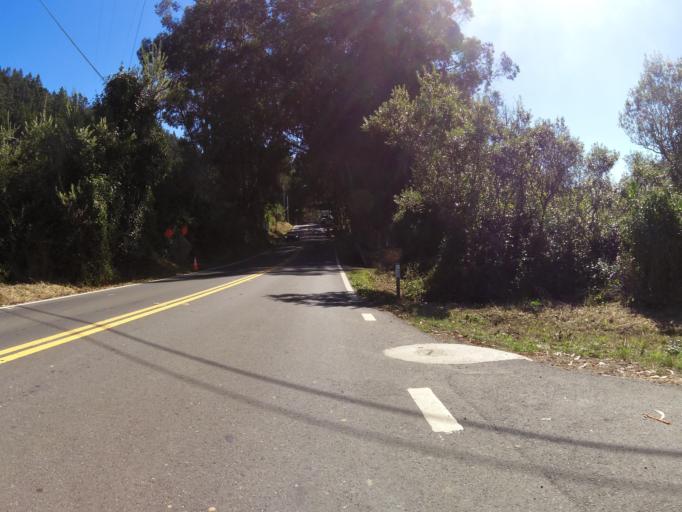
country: US
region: California
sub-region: Mendocino County
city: Fort Bragg
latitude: 39.6350
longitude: -123.7829
